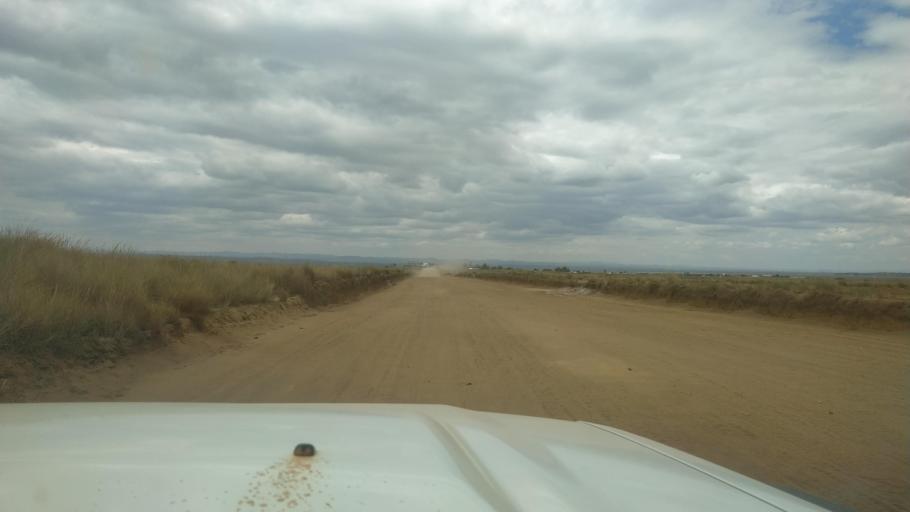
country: MG
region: Alaotra Mangoro
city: Ambatondrazaka
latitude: -17.9109
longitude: 48.2640
